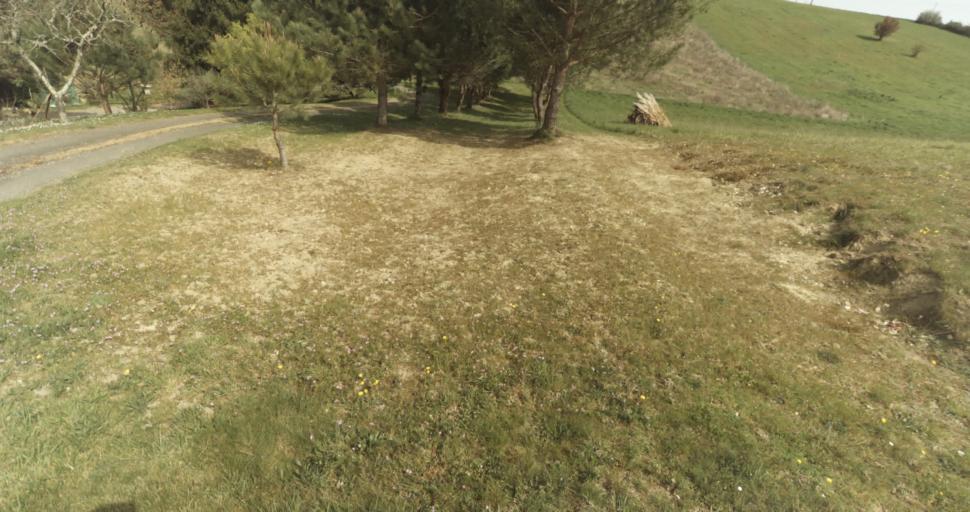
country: FR
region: Midi-Pyrenees
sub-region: Departement du Tarn-et-Garonne
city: Moissac
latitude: 44.1084
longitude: 1.0621
